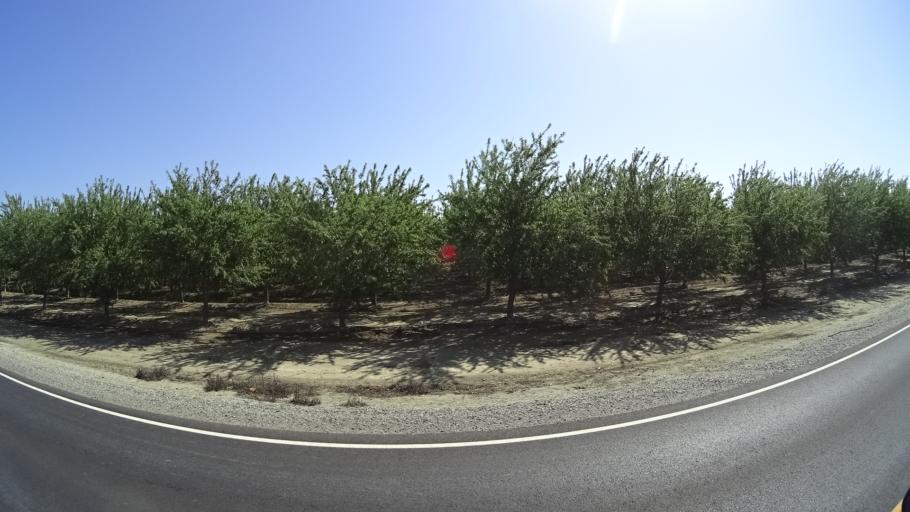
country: US
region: California
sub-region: Glenn County
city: Hamilton City
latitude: 39.6319
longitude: -122.0650
